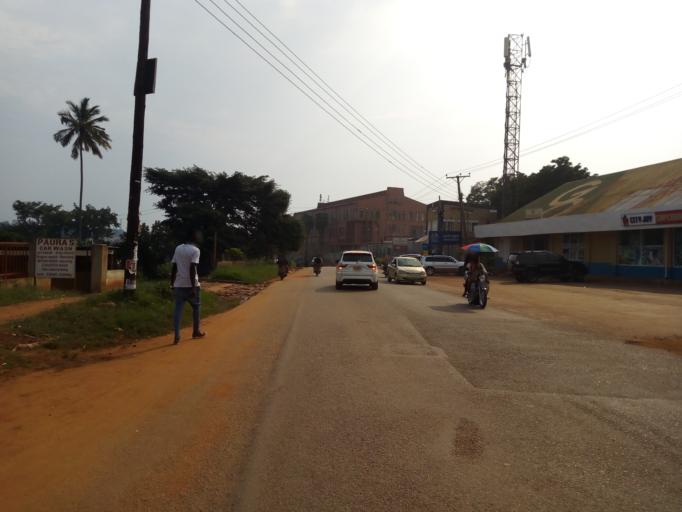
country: UG
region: Central Region
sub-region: Wakiso District
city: Kireka
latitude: 0.3190
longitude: 32.6322
